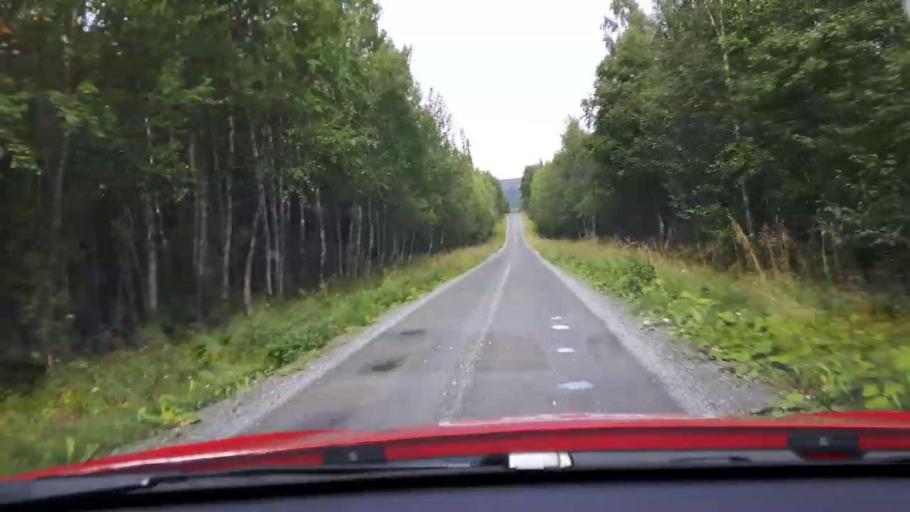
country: SE
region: Jaemtland
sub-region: Are Kommun
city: Are
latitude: 63.7947
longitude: 13.1083
